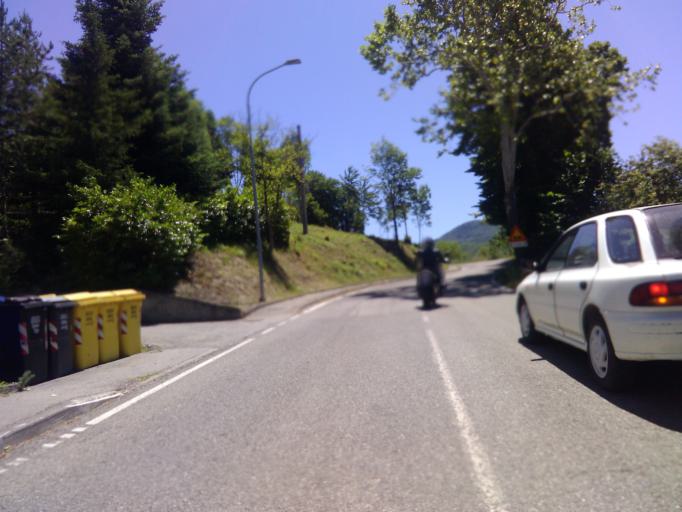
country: IT
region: Emilia-Romagna
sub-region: Provincia di Parma
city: Calestano
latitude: 44.6036
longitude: 10.1253
